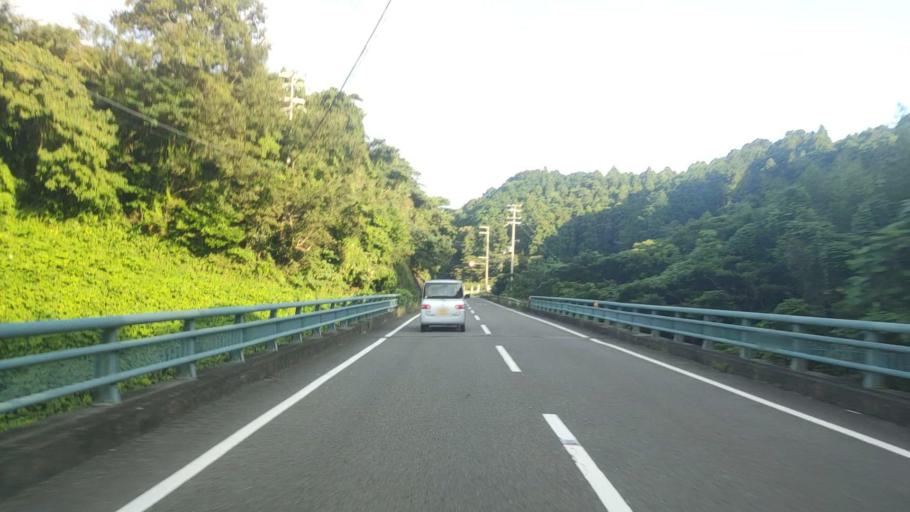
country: JP
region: Wakayama
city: Tanabe
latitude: 33.7332
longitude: 135.4327
